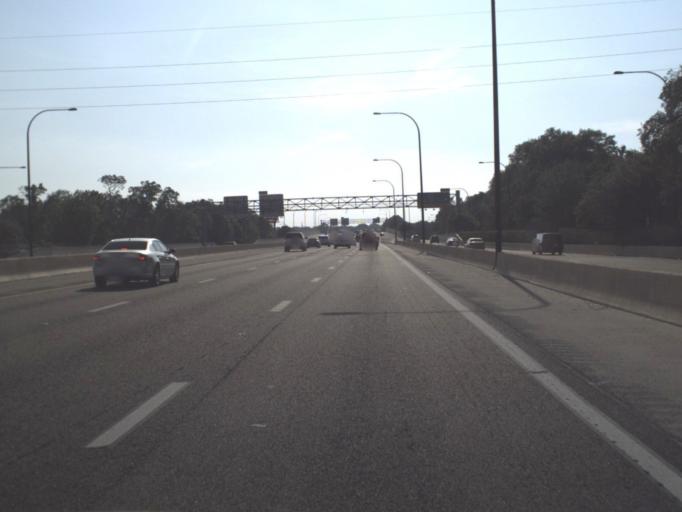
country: US
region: Florida
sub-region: Orange County
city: Pine Hills
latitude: 28.5484
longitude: -81.4414
